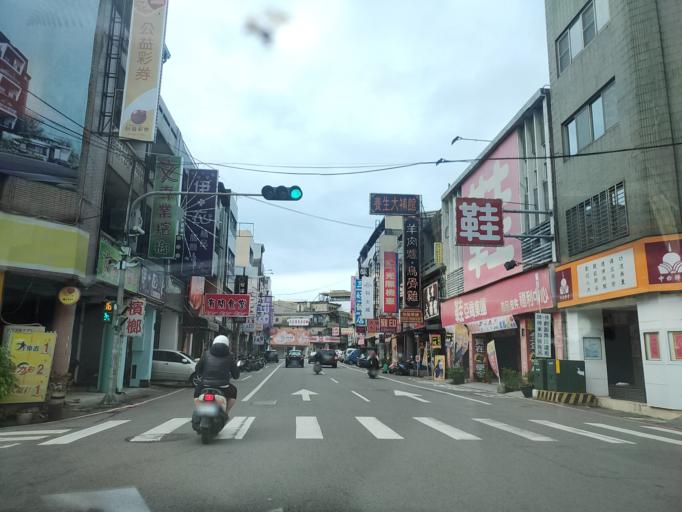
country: TW
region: Taiwan
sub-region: Miaoli
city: Miaoli
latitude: 24.5573
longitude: 120.8194
